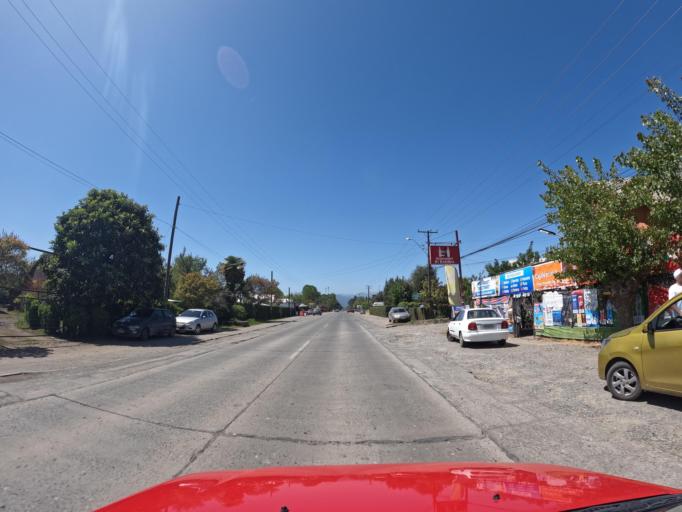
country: CL
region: Maule
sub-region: Provincia de Linares
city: Linares
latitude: -35.8321
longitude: -71.5267
